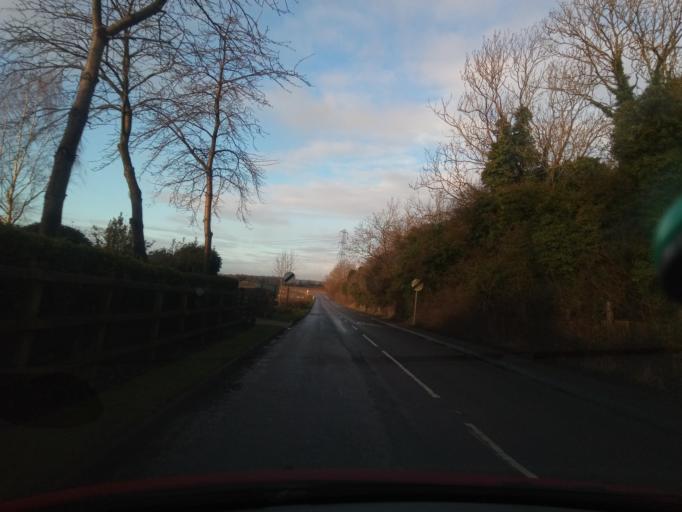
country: GB
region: England
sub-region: Derbyshire
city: Melbourne
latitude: 52.8484
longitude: -1.4120
